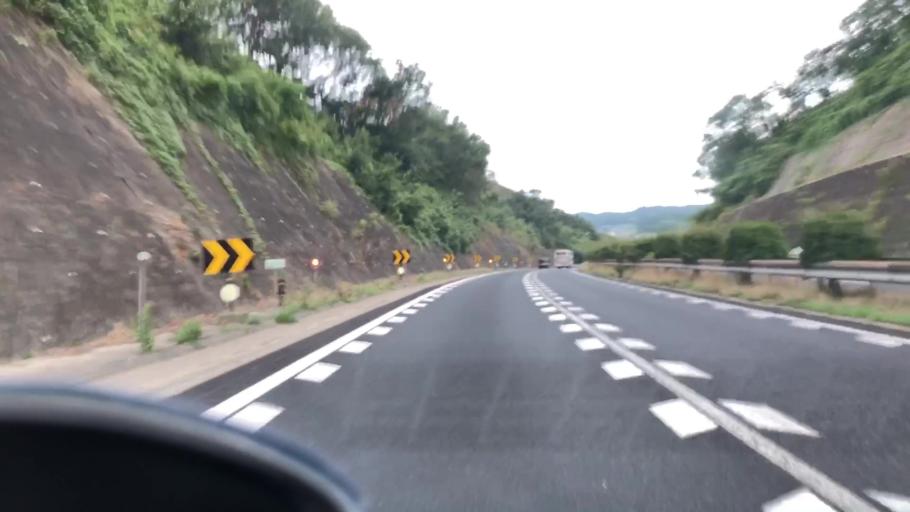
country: JP
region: Hyogo
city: Yashiro
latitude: 34.9106
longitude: 135.0547
